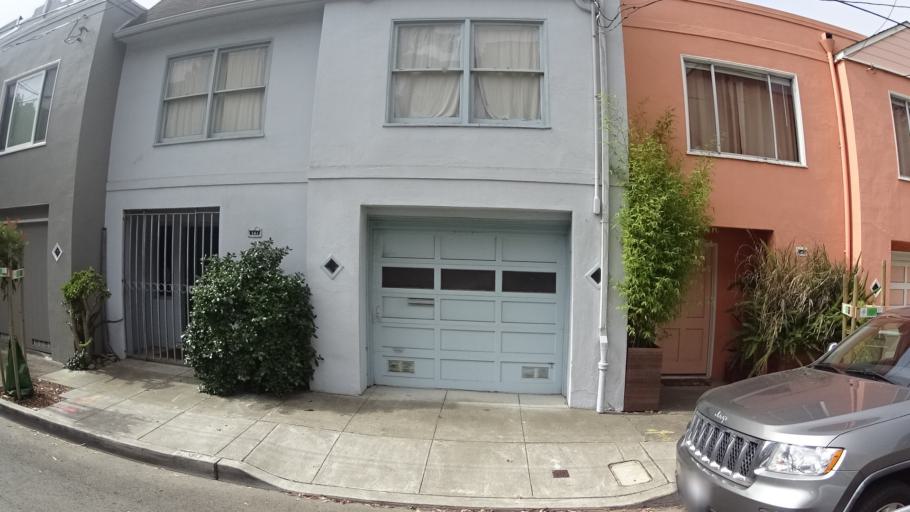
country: US
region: California
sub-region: San Francisco County
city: San Francisco
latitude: 37.7377
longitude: -122.4333
